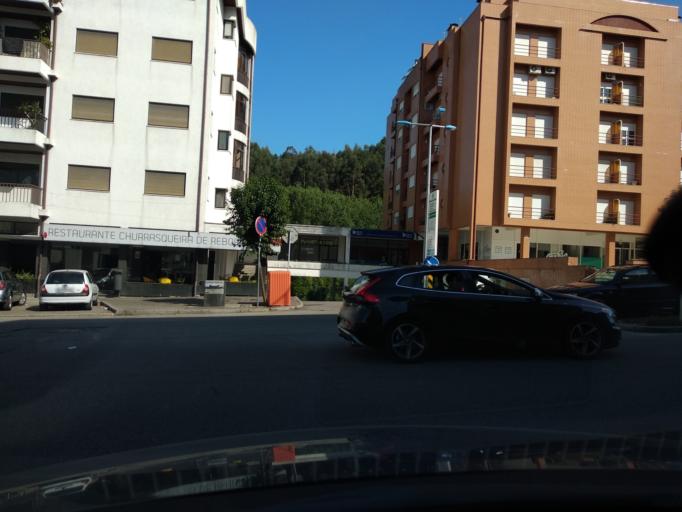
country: PT
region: Porto
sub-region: Paredes
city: Rebordosa
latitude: 41.2198
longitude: -8.4109
